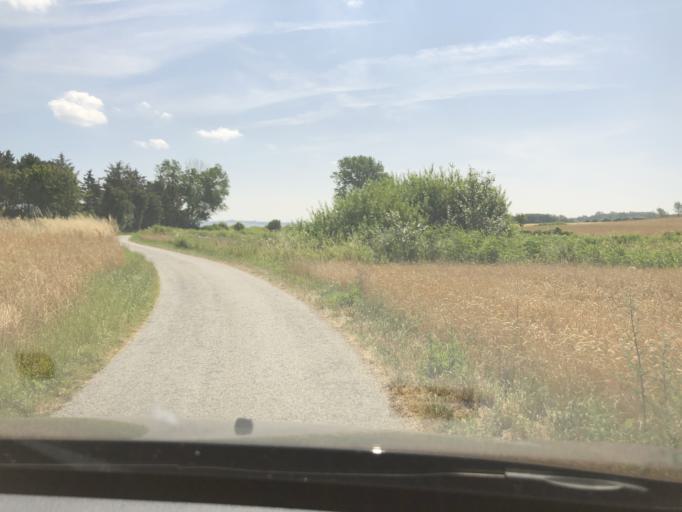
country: DK
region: South Denmark
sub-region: AEro Kommune
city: AEroskobing
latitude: 54.9132
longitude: 10.3229
